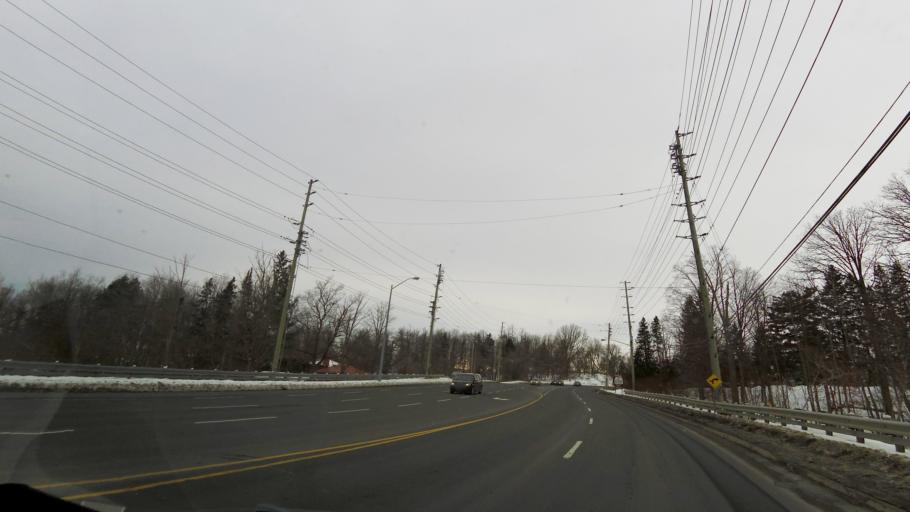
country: CA
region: Ontario
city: Vaughan
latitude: 43.8107
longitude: -79.6299
